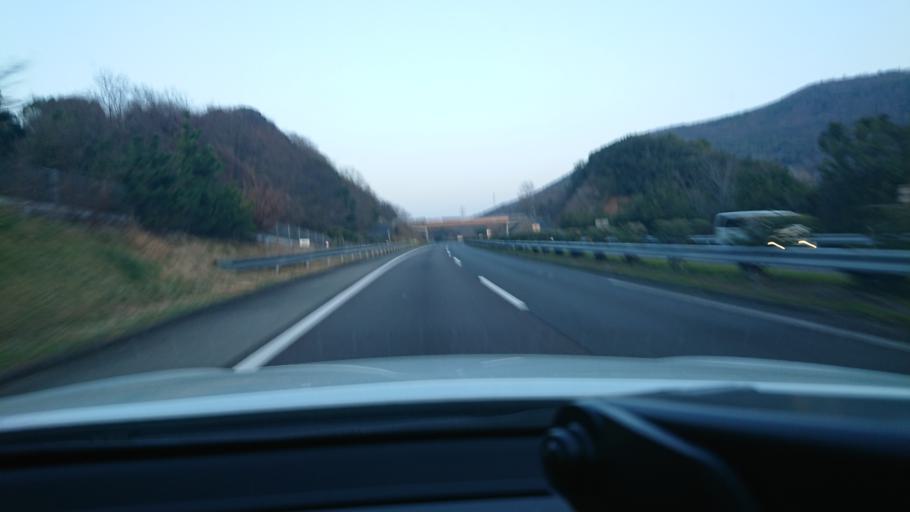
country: JP
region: Kagawa
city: Sakaidecho
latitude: 34.2762
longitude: 133.9017
